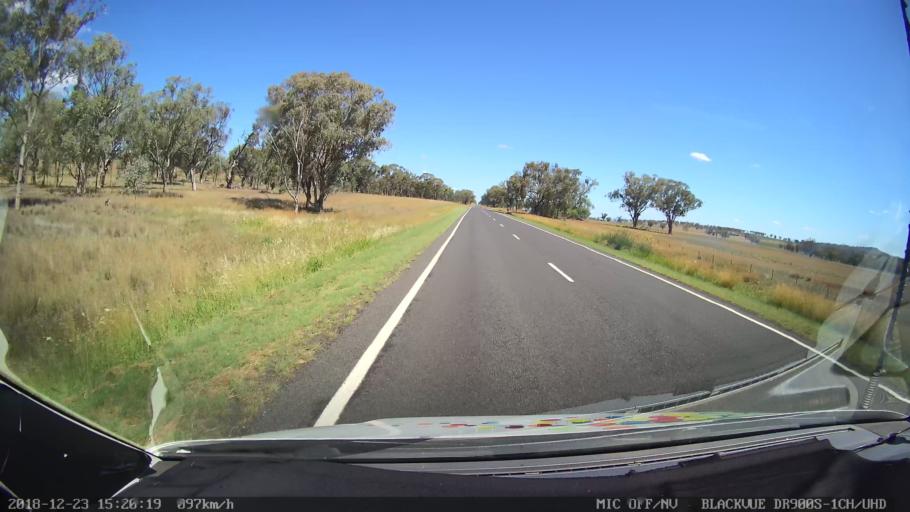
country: AU
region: New South Wales
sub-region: Tamworth Municipality
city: Manilla
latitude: -30.8411
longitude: 150.7889
